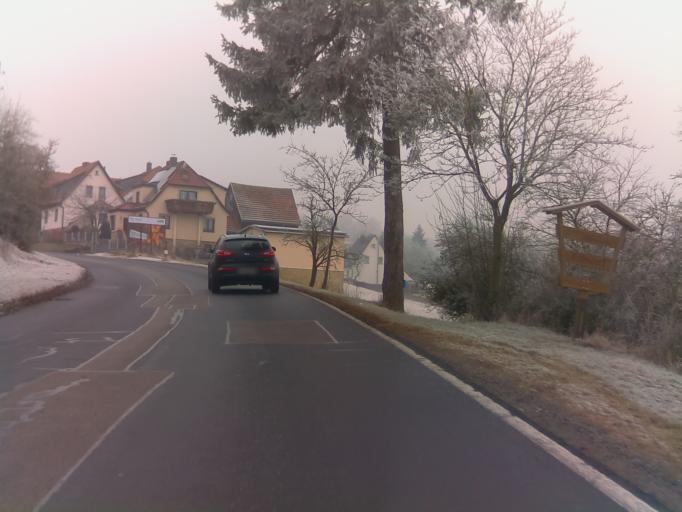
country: DE
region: Thuringia
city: Kuhndorf
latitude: 50.6092
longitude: 10.4998
